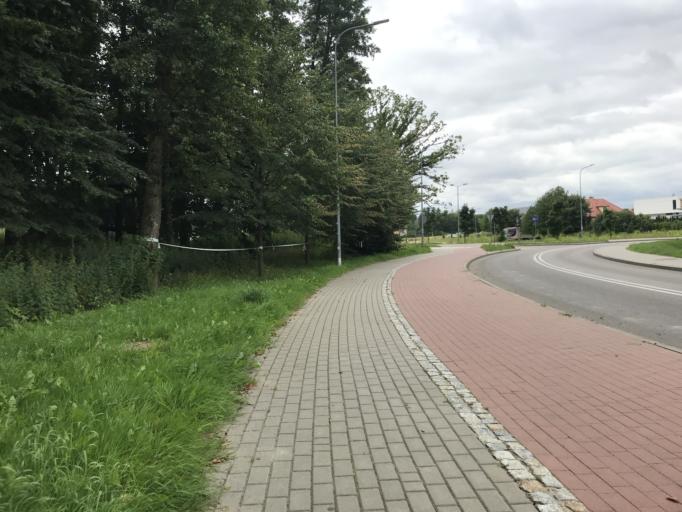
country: PL
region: Warmian-Masurian Voivodeship
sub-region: Powiat elblaski
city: Gronowo Gorne
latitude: 54.1700
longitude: 19.4417
